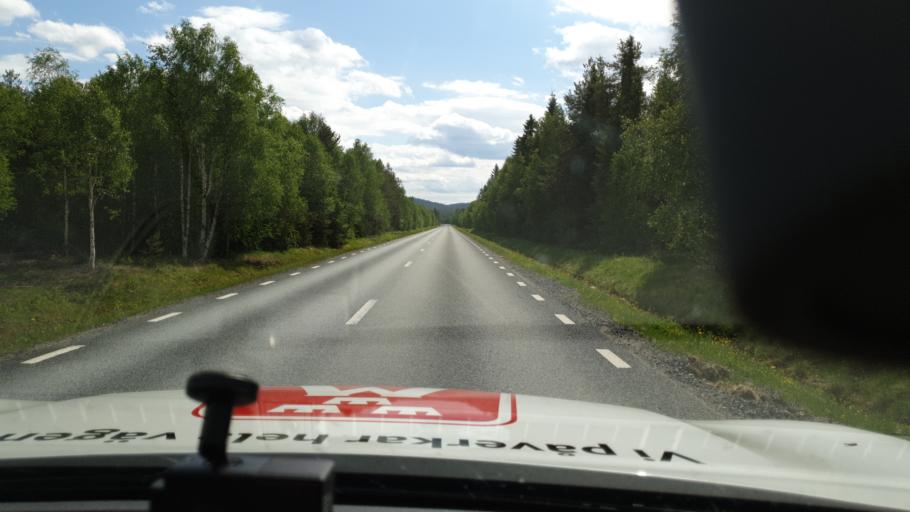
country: SE
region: Vaesterbotten
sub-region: Sorsele Kommun
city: Sorsele
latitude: 65.5204
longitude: 17.5395
